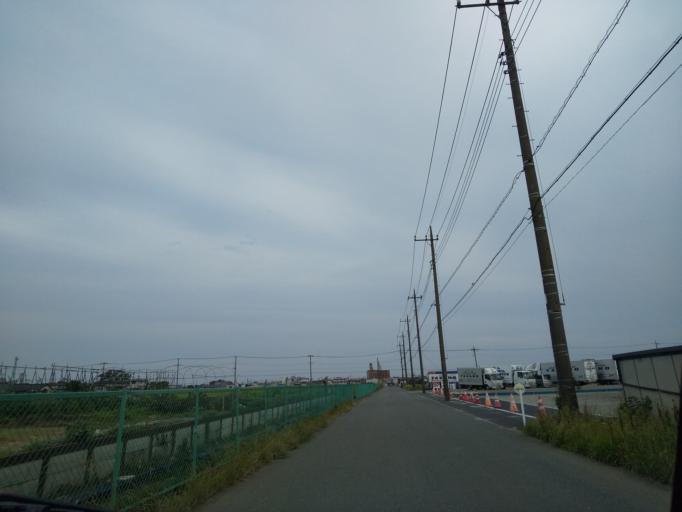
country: JP
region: Kanagawa
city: Zama
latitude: 35.4747
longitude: 139.3561
